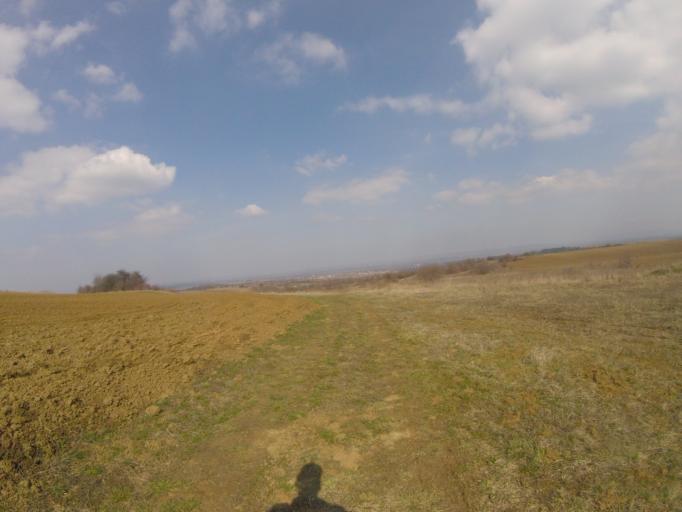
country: HU
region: Komarom-Esztergom
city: Nyergesujfalu
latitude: 47.7343
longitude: 18.5511
